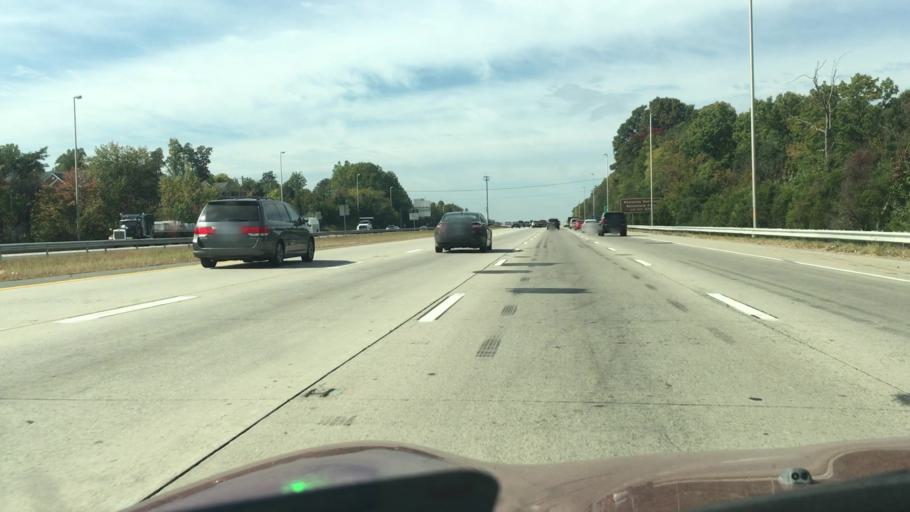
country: US
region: Virginia
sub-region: Fairfax County
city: Centreville
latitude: 38.8495
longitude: -77.4170
